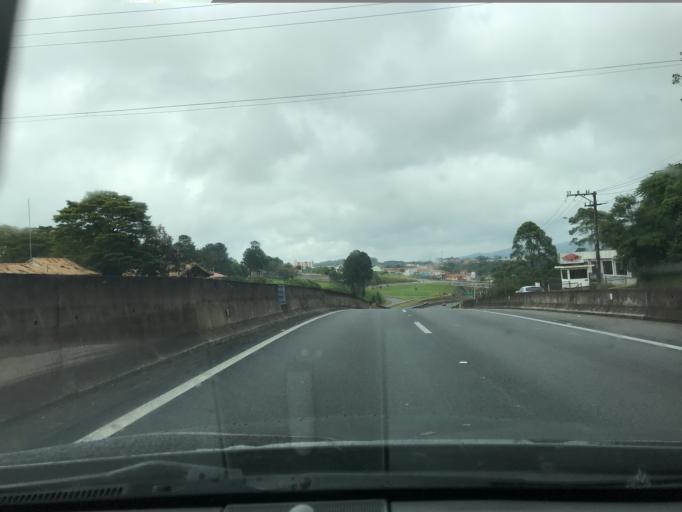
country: BR
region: Sao Paulo
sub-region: Vargem Grande Paulista
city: Vargem Grande Paulista
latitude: -23.6133
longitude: -46.9963
